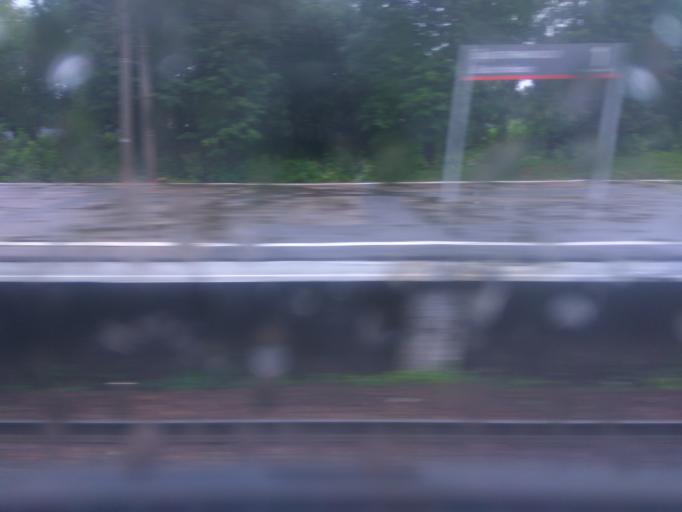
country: RU
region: Moscow
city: Zagor'ye
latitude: 55.5657
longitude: 37.6692
